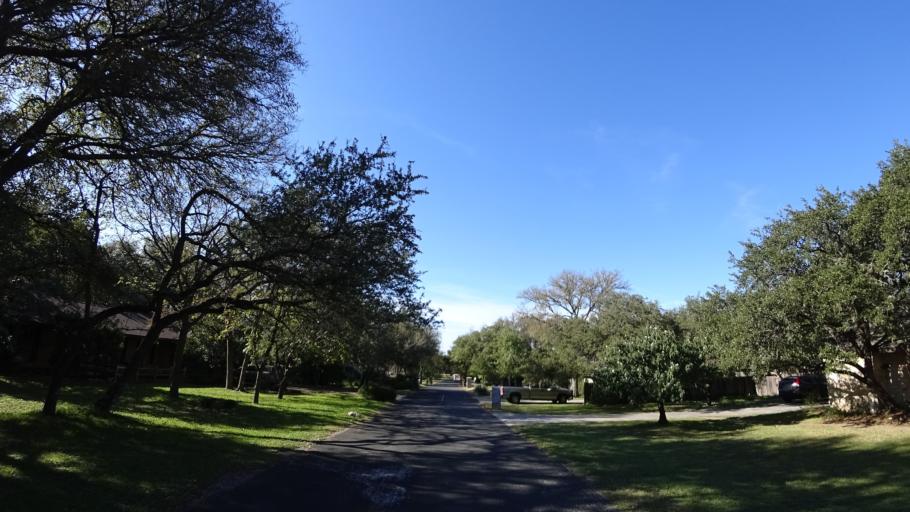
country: US
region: Texas
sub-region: Williamson County
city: Jollyville
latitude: 30.4249
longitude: -97.7809
